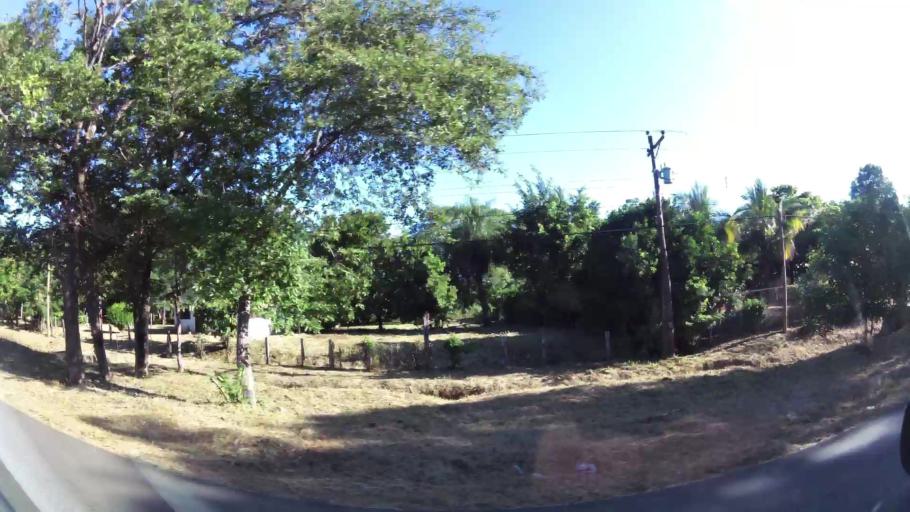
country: CR
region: Guanacaste
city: Sardinal
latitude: 10.4932
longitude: -85.6352
